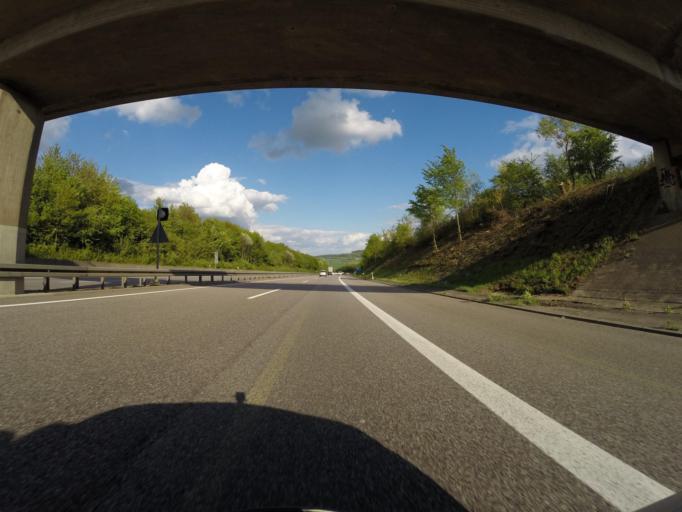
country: DE
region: Saarland
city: Orscholz
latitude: 49.4529
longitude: 6.5289
